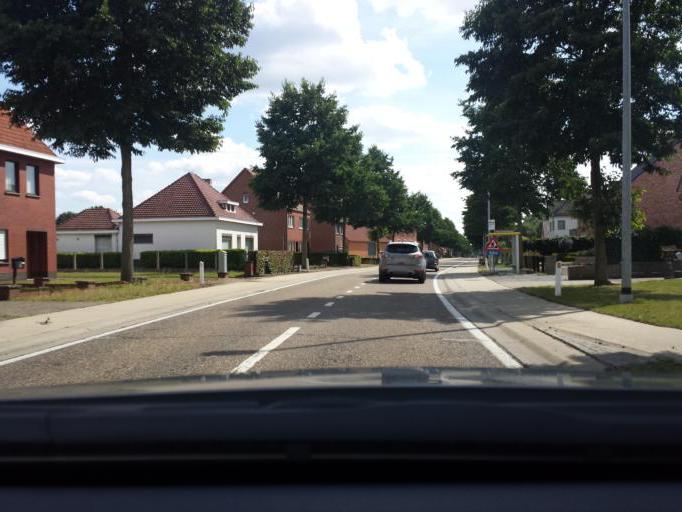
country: BE
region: Flanders
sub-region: Provincie Limburg
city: Beringen
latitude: 51.0411
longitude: 5.2159
